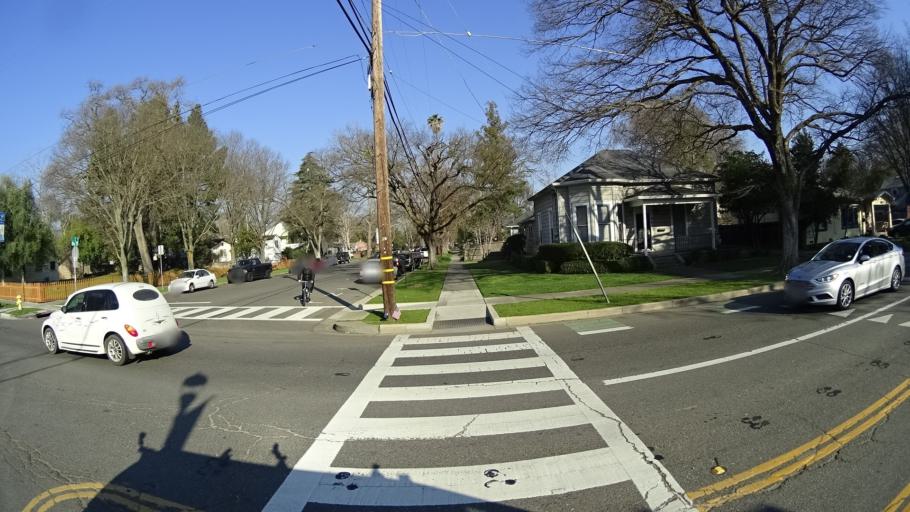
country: US
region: California
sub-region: Yolo County
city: Davis
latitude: 38.5470
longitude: -121.7433
